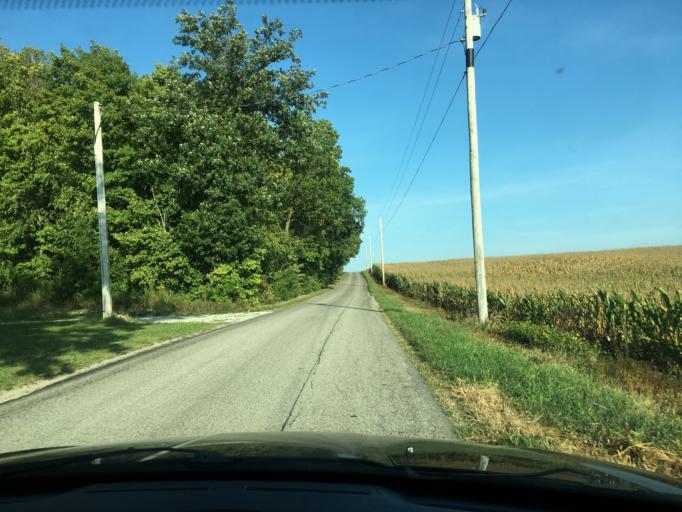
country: US
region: Ohio
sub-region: Logan County
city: West Liberty
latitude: 40.2988
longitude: -83.7364
